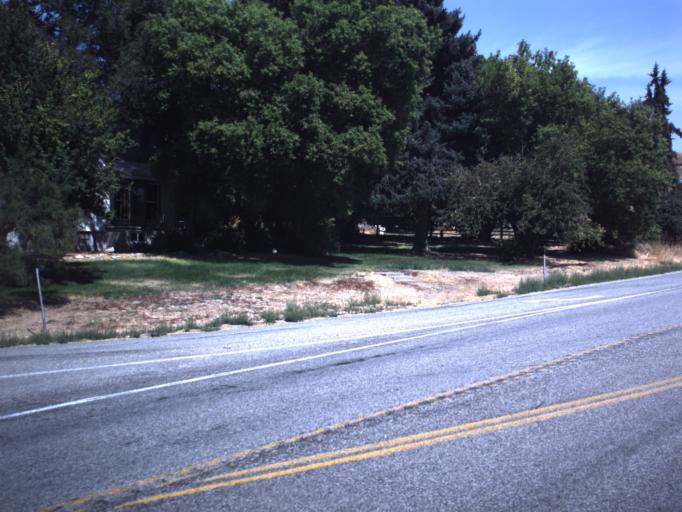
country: US
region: Utah
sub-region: Cache County
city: Mendon
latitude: 41.7950
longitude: -112.0398
